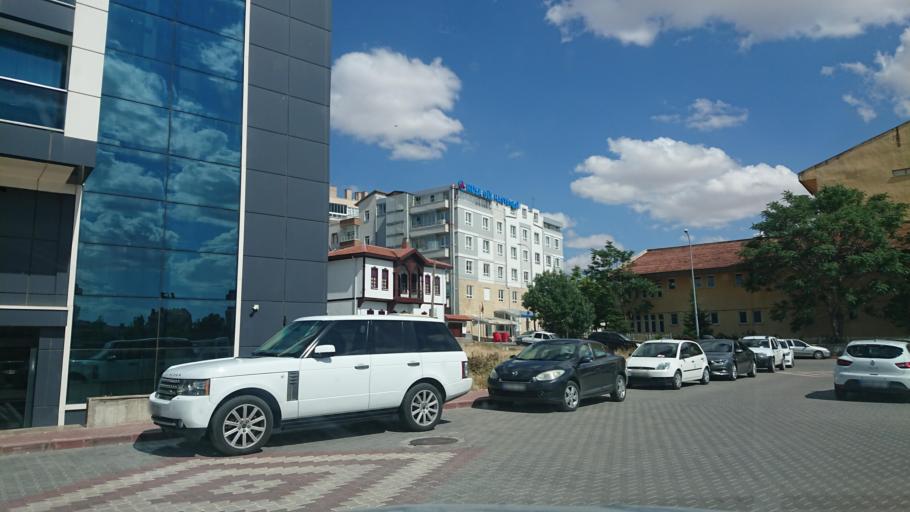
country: TR
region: Kirsehir
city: Kirsehir
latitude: 39.1493
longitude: 34.1584
